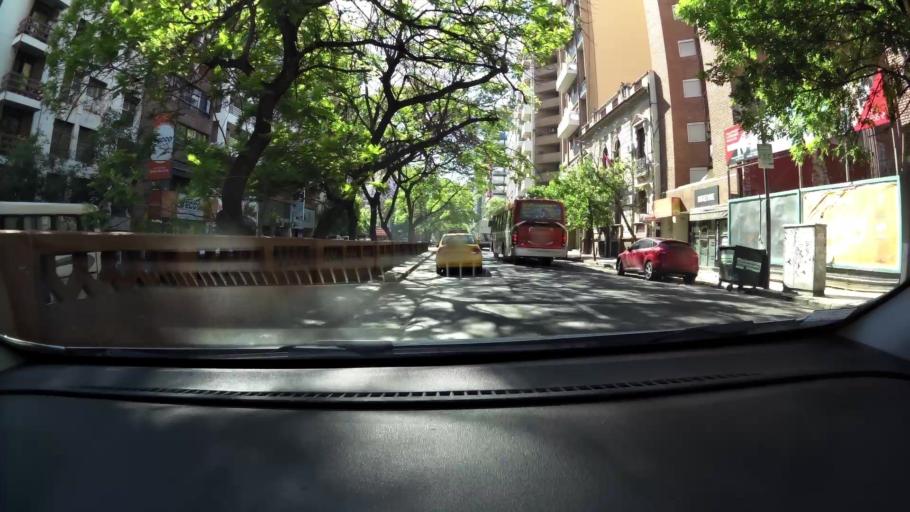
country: AR
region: Cordoba
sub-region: Departamento de Capital
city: Cordoba
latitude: -31.4216
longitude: -64.1832
